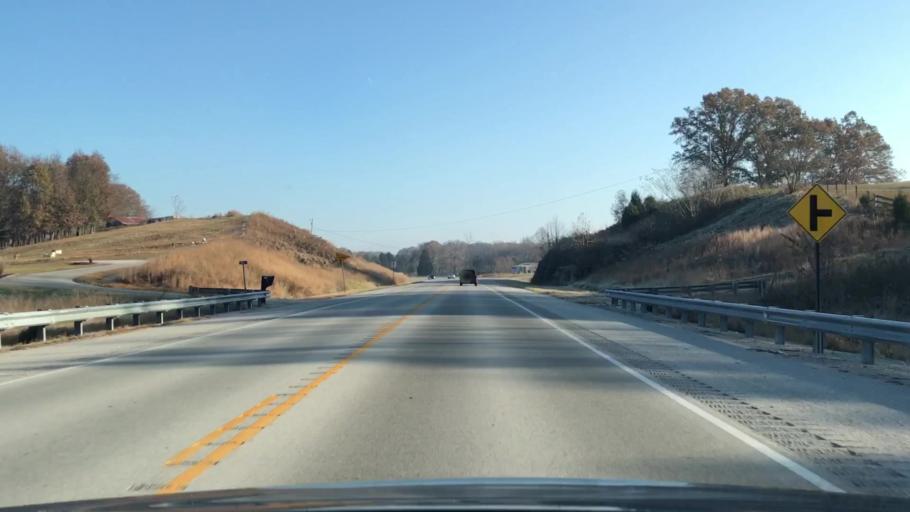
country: US
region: Kentucky
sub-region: Edmonson County
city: Brownsville
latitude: 37.1445
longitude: -86.2250
